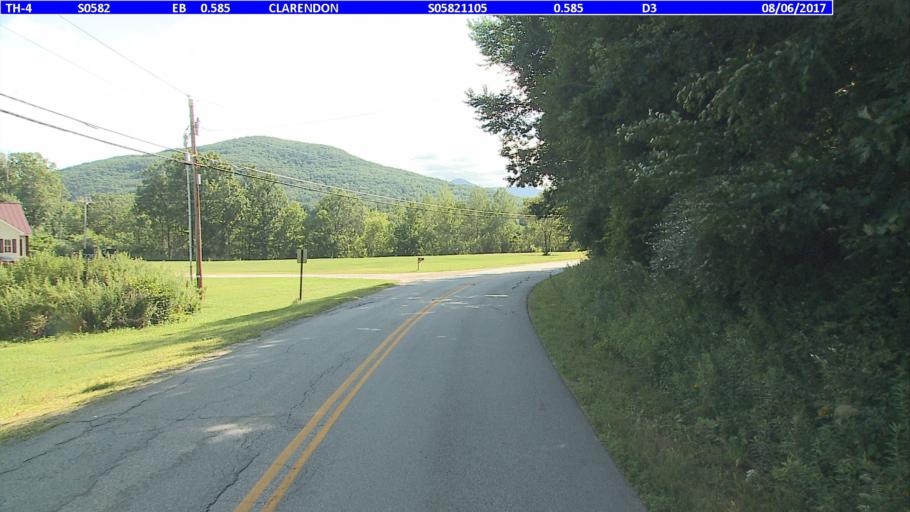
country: US
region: Vermont
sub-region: Rutland County
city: Rutland
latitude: 43.5683
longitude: -72.9521
